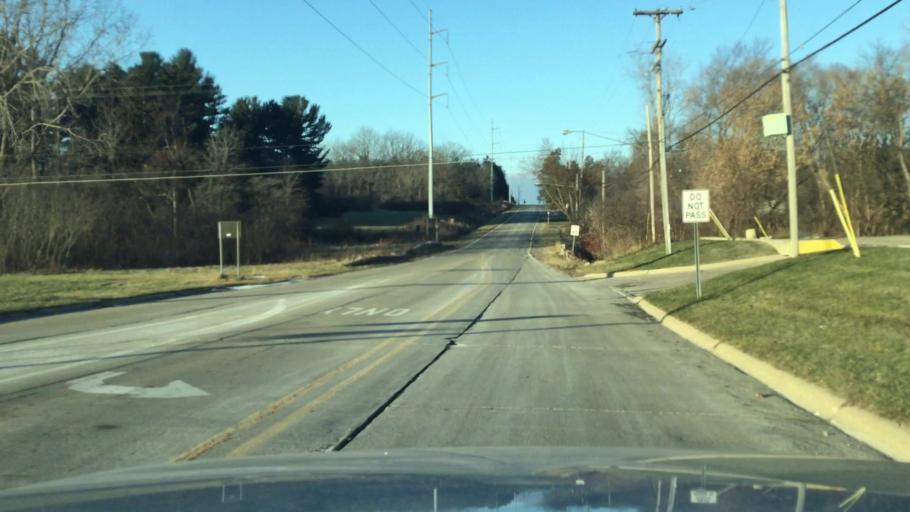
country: US
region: Michigan
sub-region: Genesee County
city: Flushing
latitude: 43.0459
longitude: -83.7731
